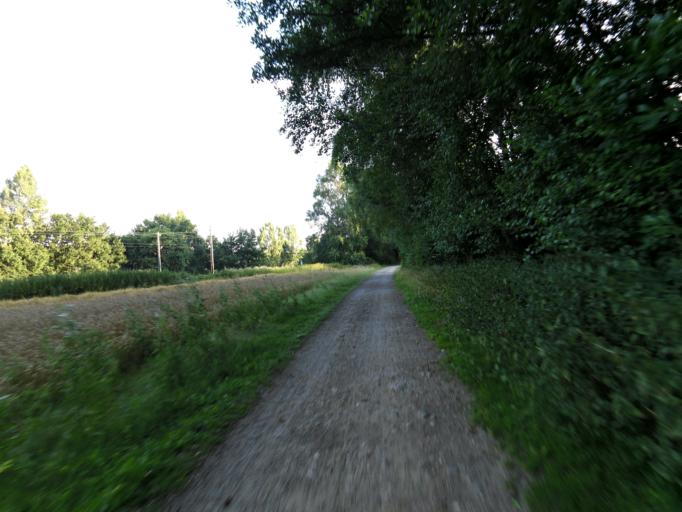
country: DE
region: North Rhine-Westphalia
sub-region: Regierungsbezirk Koln
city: Herzogenrath
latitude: 50.9040
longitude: 6.0829
